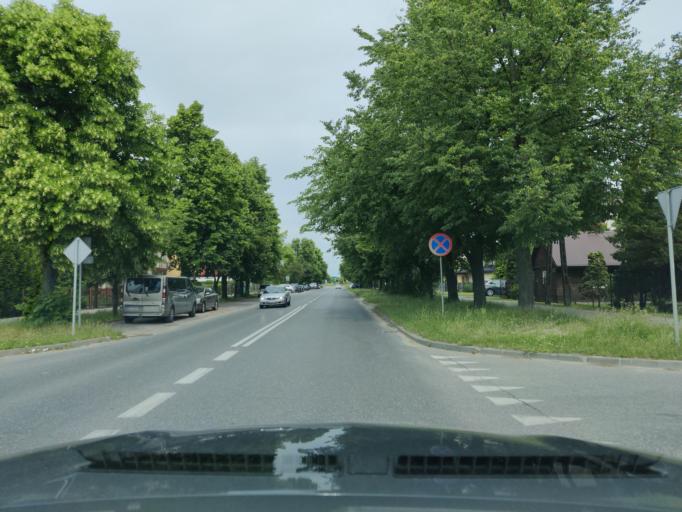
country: PL
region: Masovian Voivodeship
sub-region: Powiat wyszkowski
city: Wyszkow
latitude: 52.6038
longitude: 21.4552
